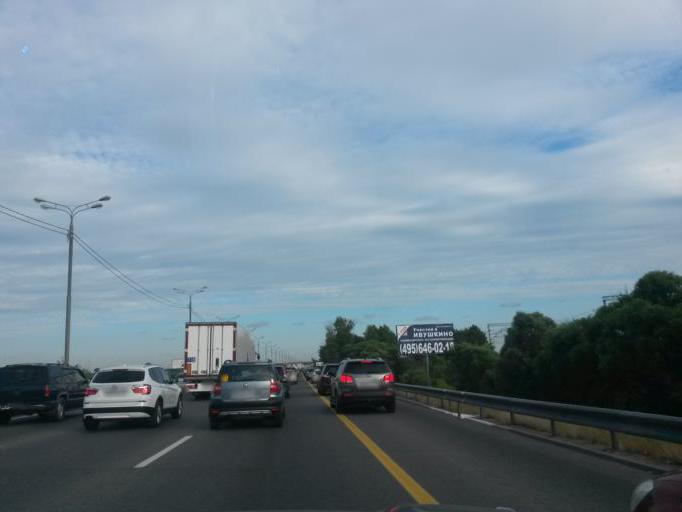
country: RU
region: Moskovskaya
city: Yam
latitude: 55.5102
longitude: 37.7169
